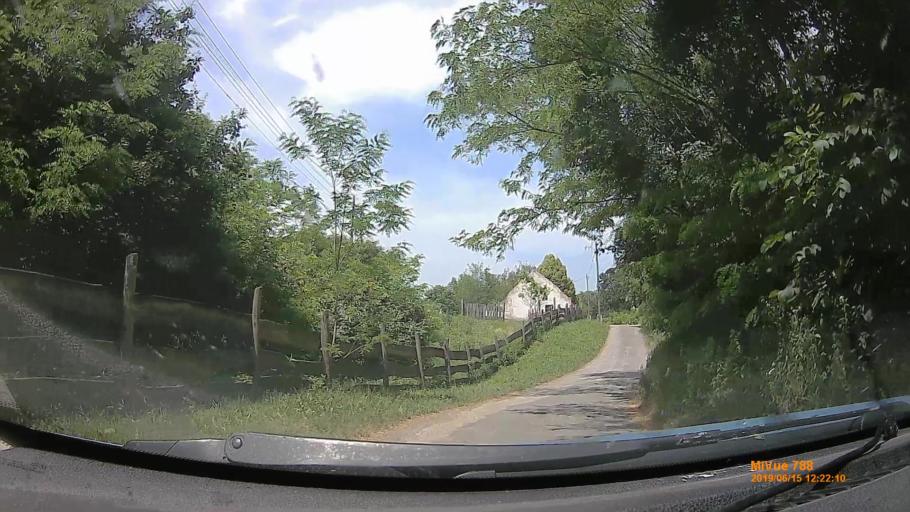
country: HU
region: Baranya
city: Buekkoesd
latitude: 46.1088
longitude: 18.0078
